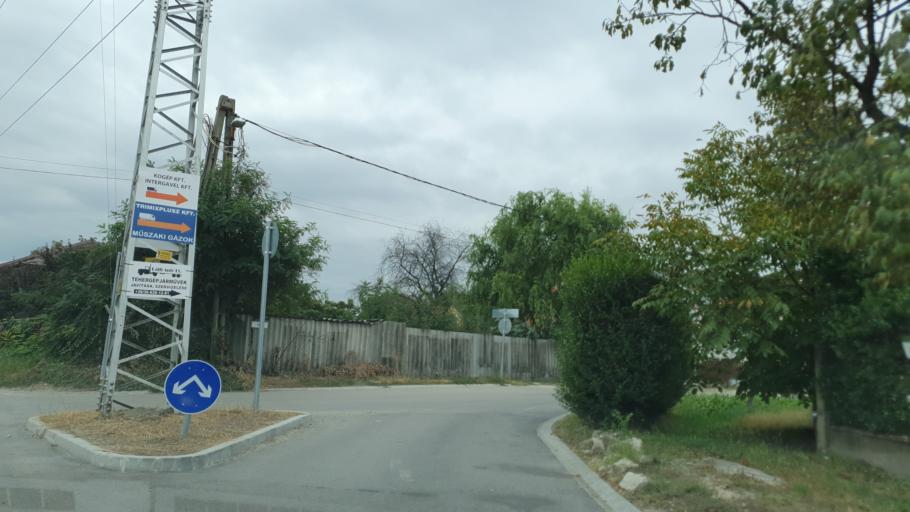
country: HU
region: Budapest
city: Budapest XXIII. keruelet
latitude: 47.3911
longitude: 19.0940
